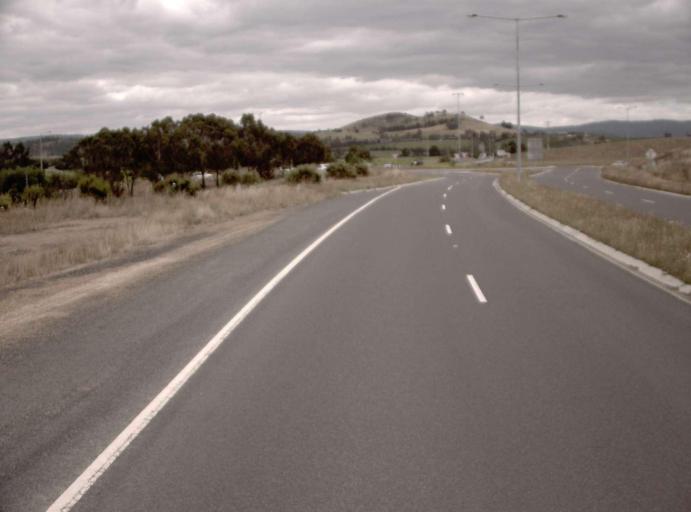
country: AU
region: Victoria
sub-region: Yarra Ranges
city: Yarra Glen
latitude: -37.6479
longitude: 145.3969
